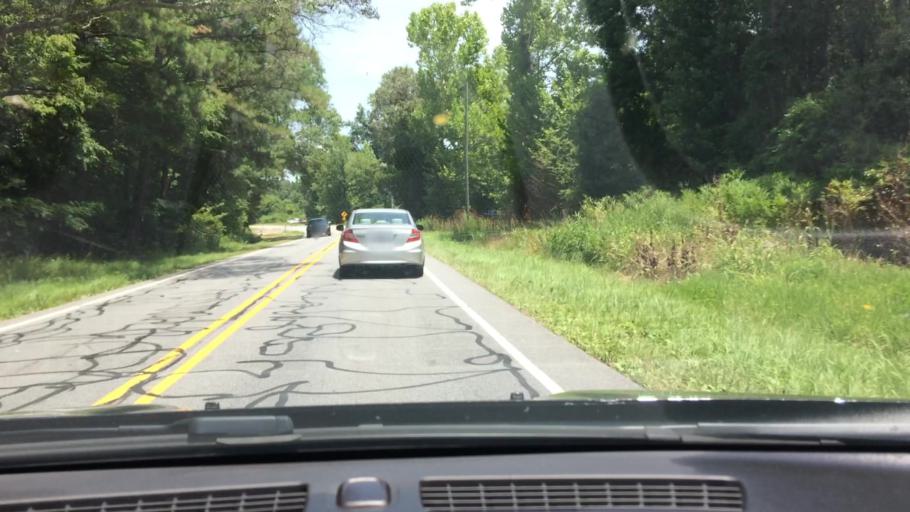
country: US
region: North Carolina
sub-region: Beaufort County
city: Washington
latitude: 35.5968
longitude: -77.1594
